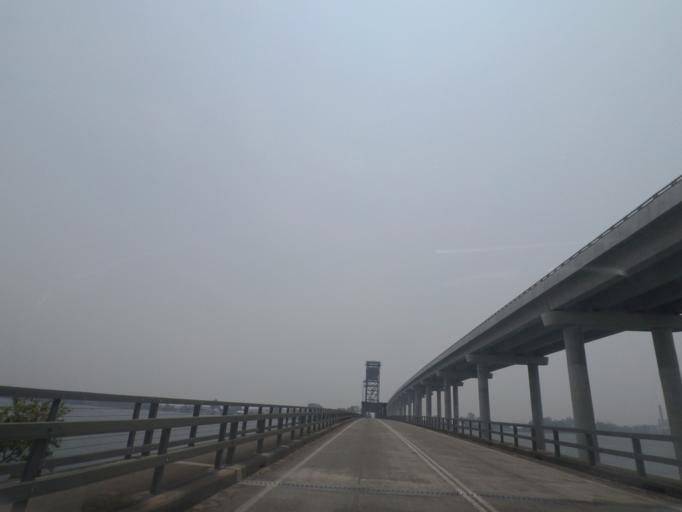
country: AU
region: New South Wales
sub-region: Clarence Valley
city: Maclean
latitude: -29.4329
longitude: 153.2407
